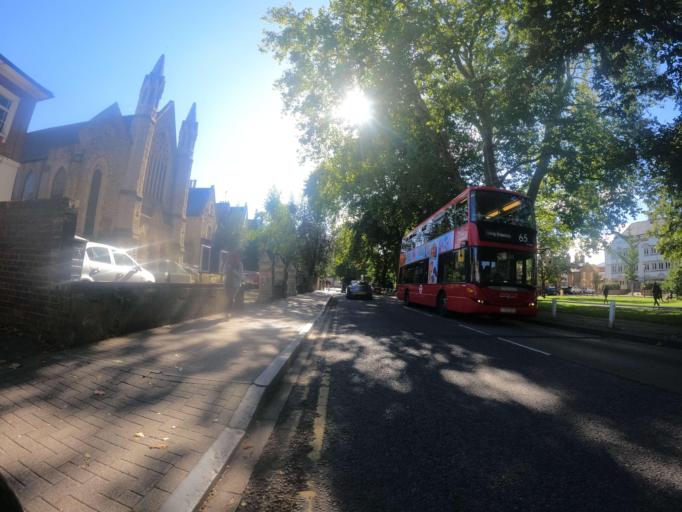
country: GB
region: England
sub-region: Greater London
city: Ealing
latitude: 51.5101
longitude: -0.3055
